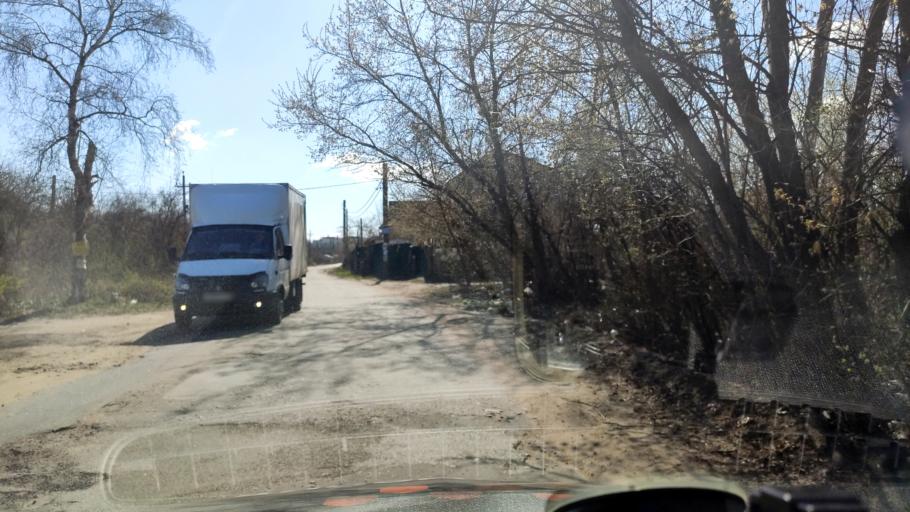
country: RU
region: Voronezj
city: Maslovka
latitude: 51.5889
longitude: 39.1636
